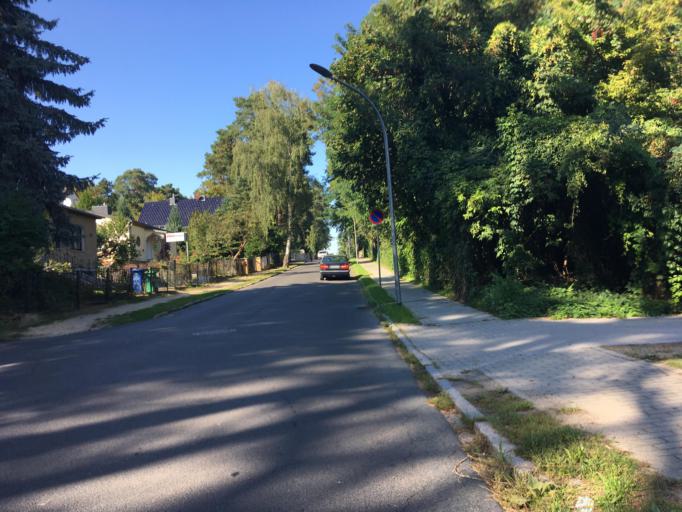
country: DE
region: Brandenburg
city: Wildau
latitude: 52.3321
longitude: 13.6347
